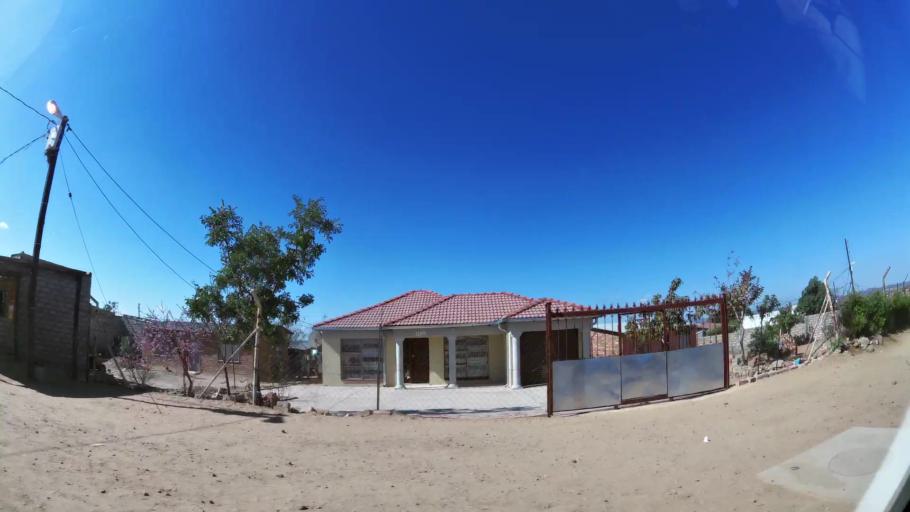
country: ZA
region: Limpopo
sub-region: Capricorn District Municipality
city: Polokwane
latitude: -23.8842
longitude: 29.4089
